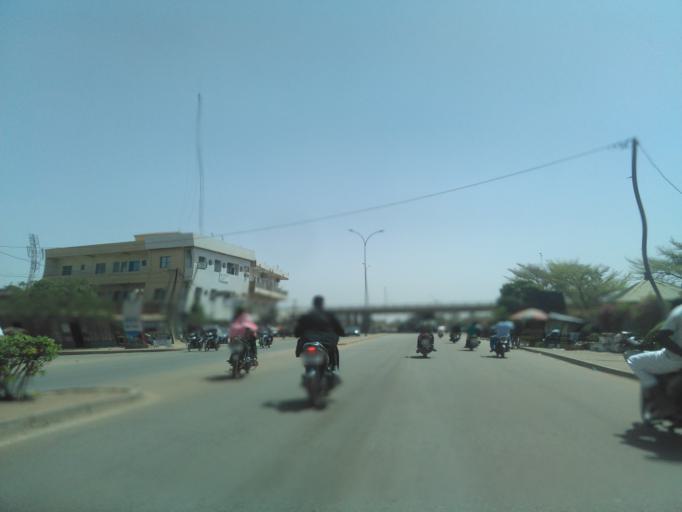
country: BF
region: Centre
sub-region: Kadiogo Province
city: Ouagadougou
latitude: 12.3523
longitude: -1.5568
